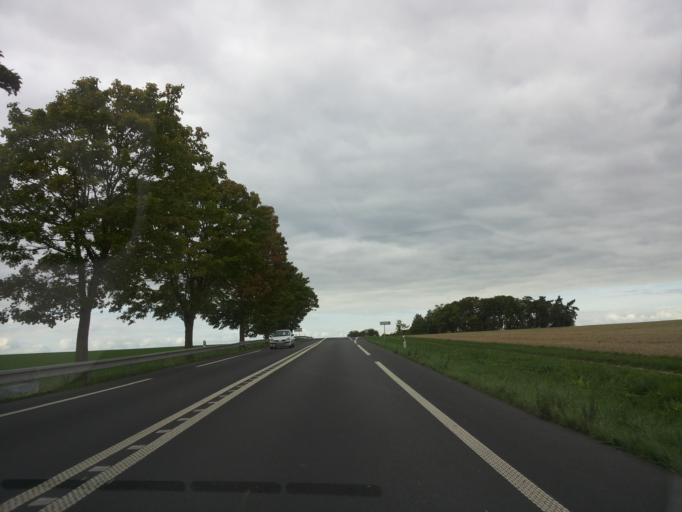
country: FR
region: Champagne-Ardenne
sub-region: Departement de la Marne
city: Verzy
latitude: 49.1433
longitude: 4.2208
